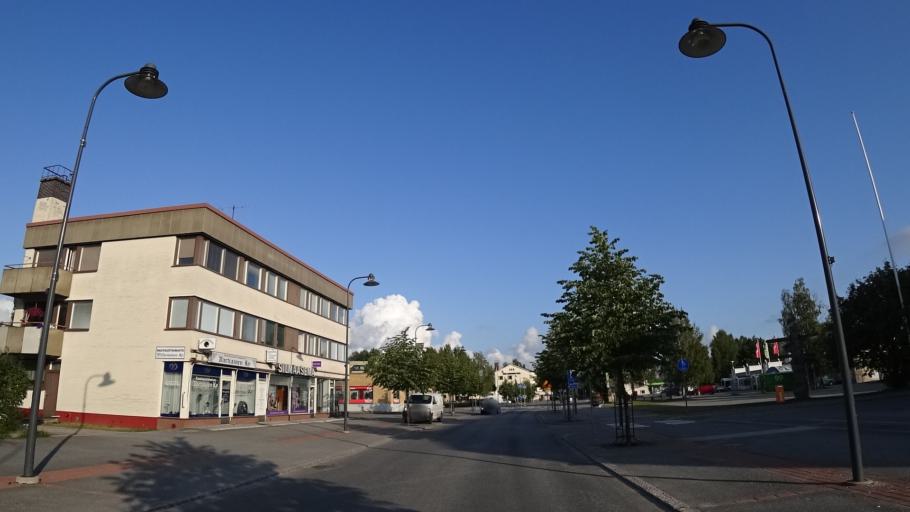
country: FI
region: North Karelia
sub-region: Pielisen Karjala
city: Lieksa
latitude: 63.3176
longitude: 30.0293
